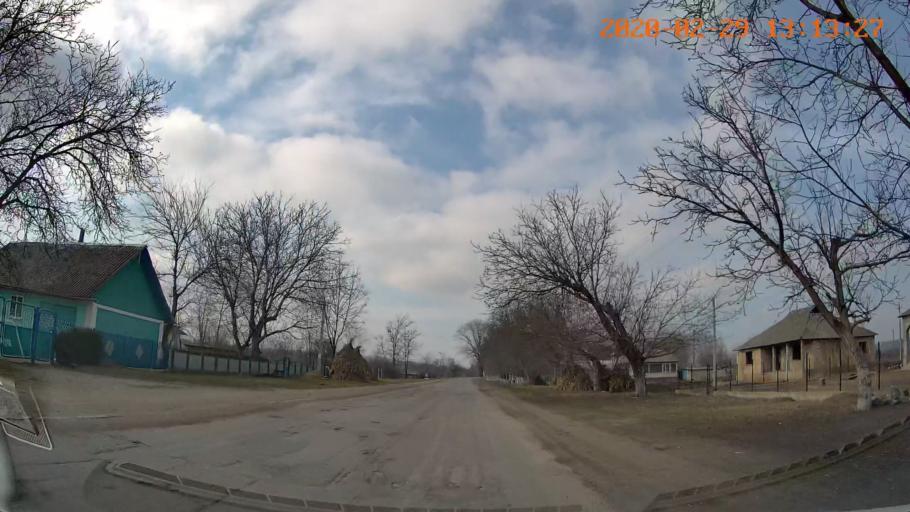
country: MD
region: Telenesti
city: Camenca
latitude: 48.0143
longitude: 28.6840
